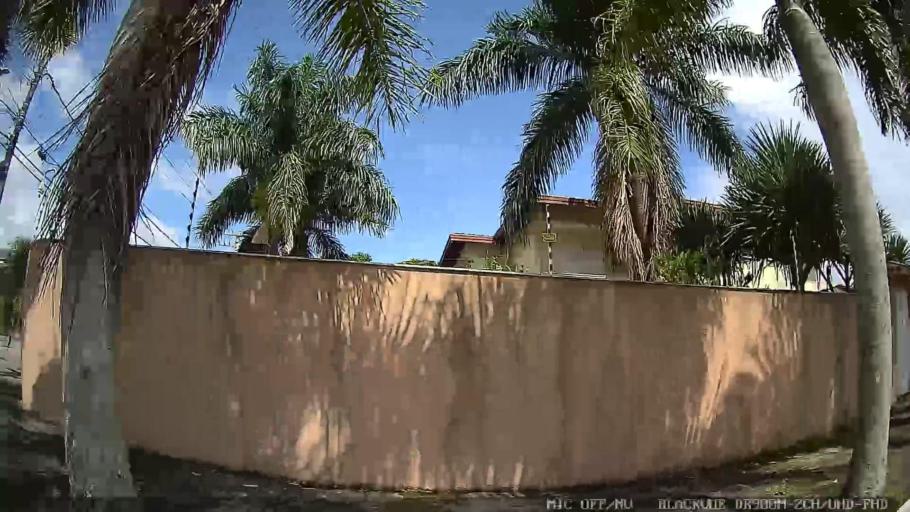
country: BR
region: Sao Paulo
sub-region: Caraguatatuba
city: Caraguatatuba
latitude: -23.6292
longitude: -45.4198
